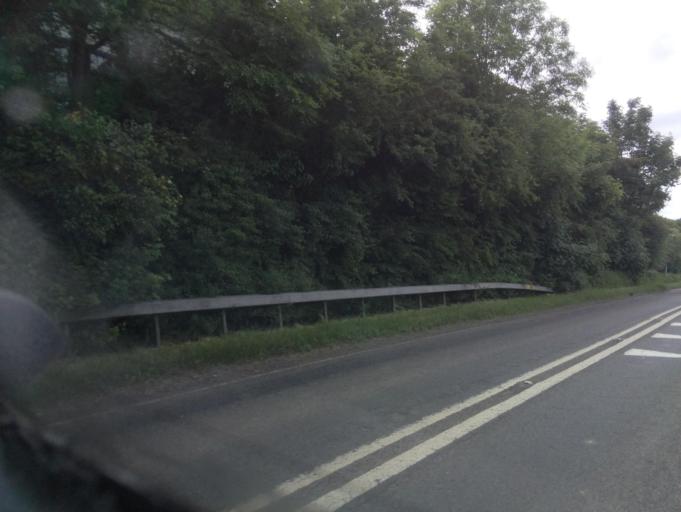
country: GB
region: England
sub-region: Worcestershire
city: Kempsey
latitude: 52.1594
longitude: -2.1585
